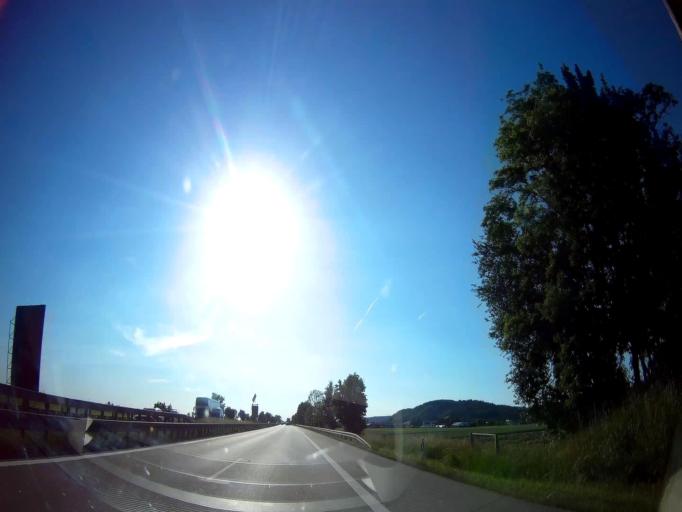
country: DE
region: Bavaria
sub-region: Lower Bavaria
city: Kirchroth
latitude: 48.9626
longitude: 12.5324
